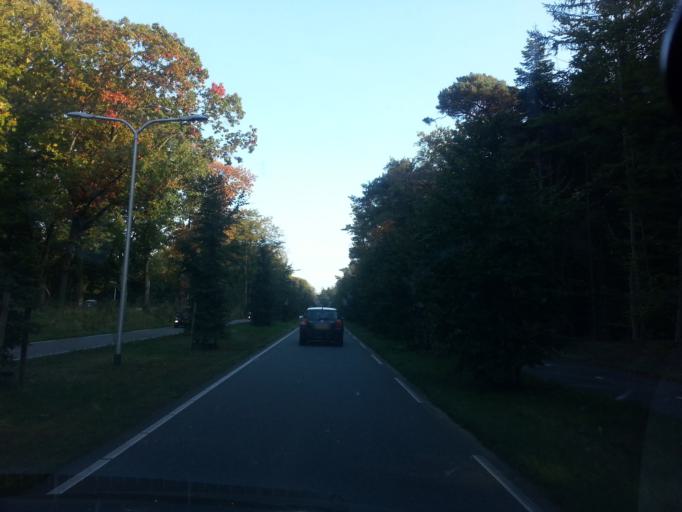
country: NL
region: Utrecht
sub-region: Gemeente Zeist
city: Zeist
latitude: 52.0960
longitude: 5.2747
